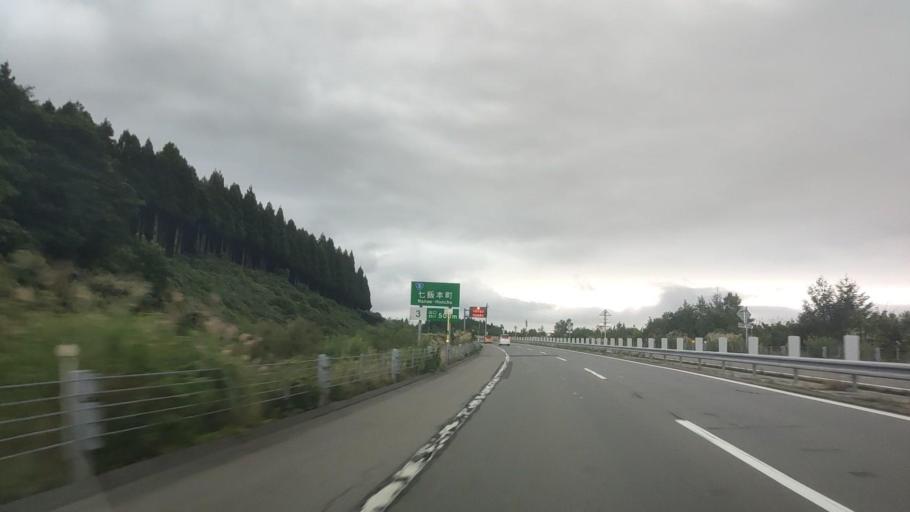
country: JP
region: Hokkaido
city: Nanae
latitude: 41.9036
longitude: 140.6987
